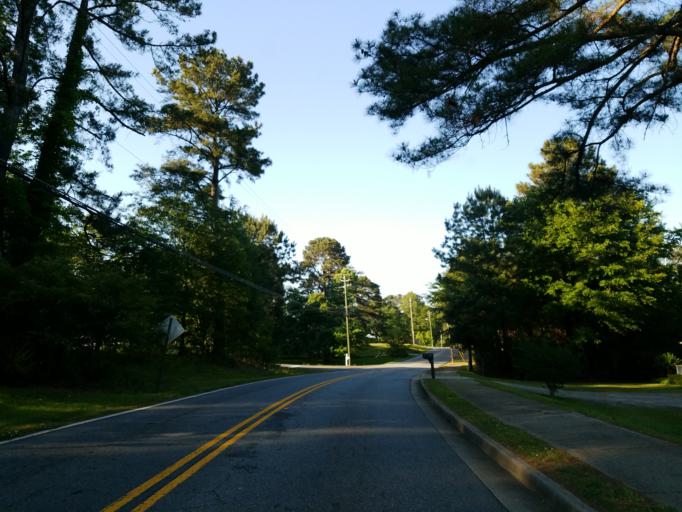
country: US
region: Georgia
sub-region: Cobb County
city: Mableton
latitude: 33.8229
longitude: -84.5545
